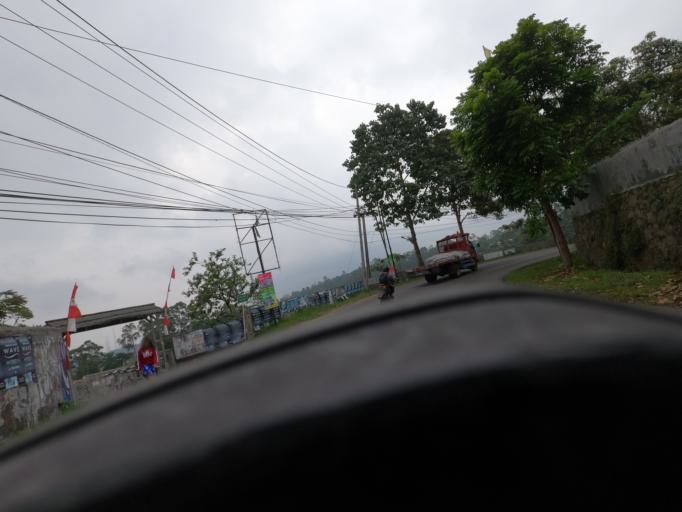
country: ID
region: West Java
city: Lembang
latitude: -6.8023
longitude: 107.5771
